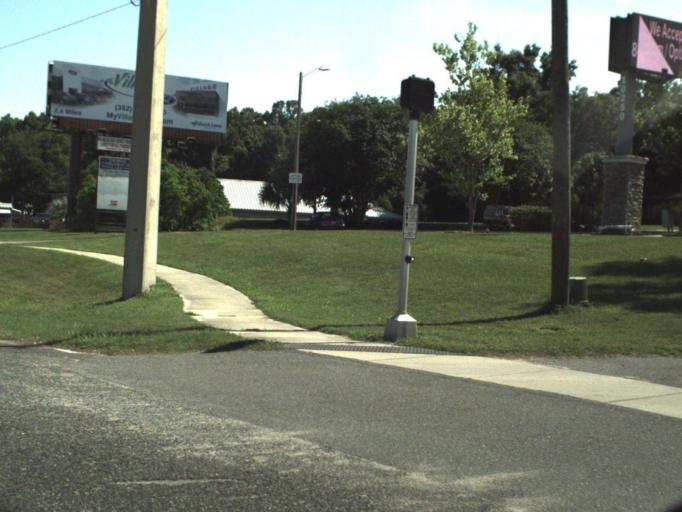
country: US
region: Florida
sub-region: Marion County
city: Belleview
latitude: 29.0735
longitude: -82.0728
